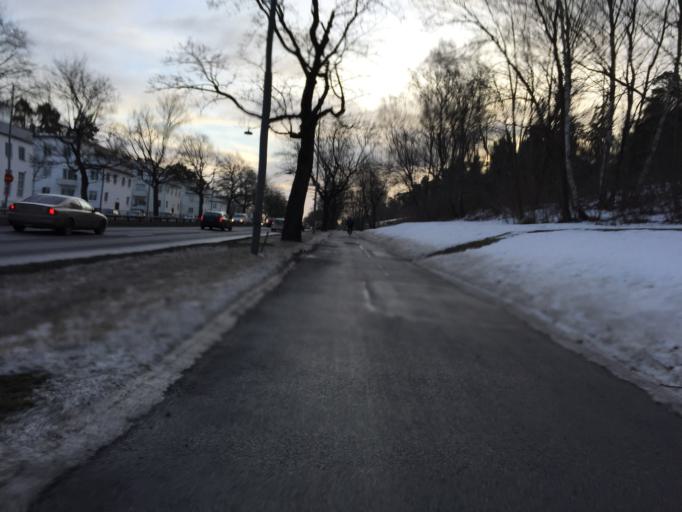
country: SE
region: Stockholm
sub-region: Stockholms Kommun
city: Bromma
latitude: 59.3361
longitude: 17.9586
